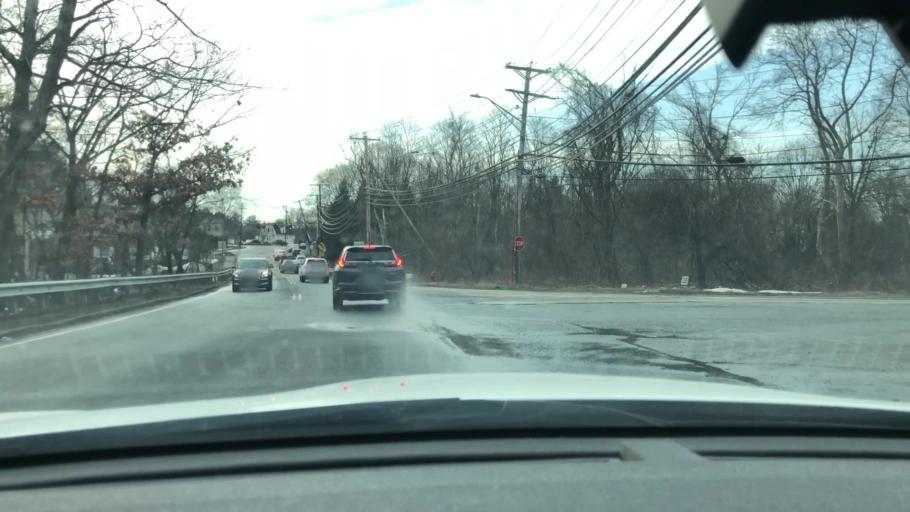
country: US
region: Massachusetts
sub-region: Middlesex County
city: Chelmsford
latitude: 42.5988
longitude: -71.3382
